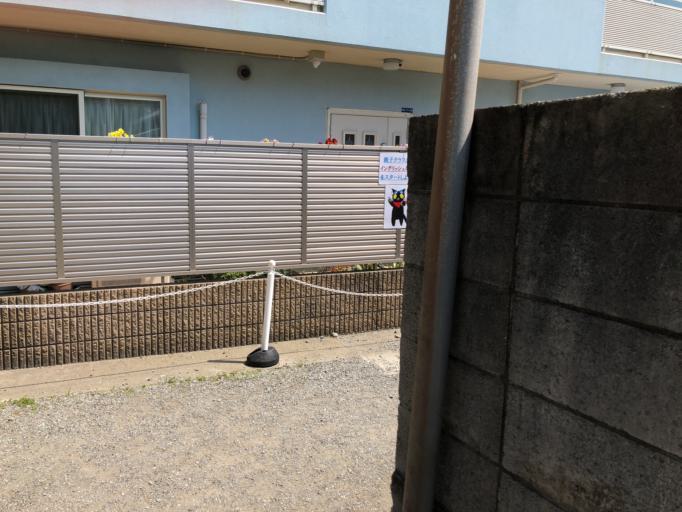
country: JP
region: Kanagawa
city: Kamakura
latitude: 35.3186
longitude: 139.5493
